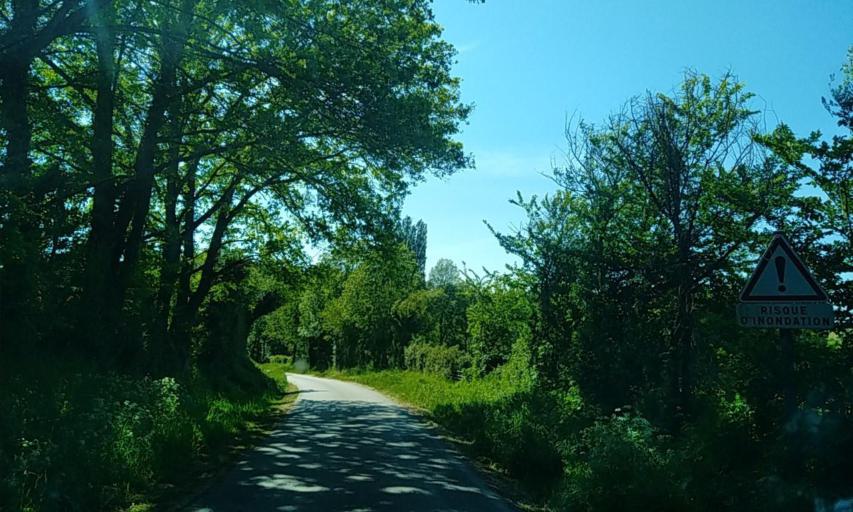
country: FR
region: Poitou-Charentes
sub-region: Departement des Deux-Sevres
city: Chiche
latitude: 46.7880
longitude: -0.3876
